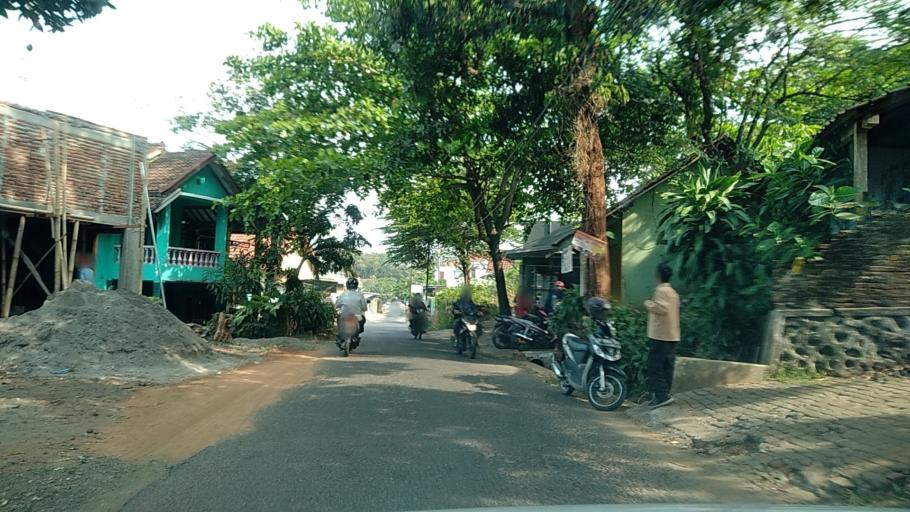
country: ID
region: Central Java
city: Semarang
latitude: -7.0504
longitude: 110.3140
